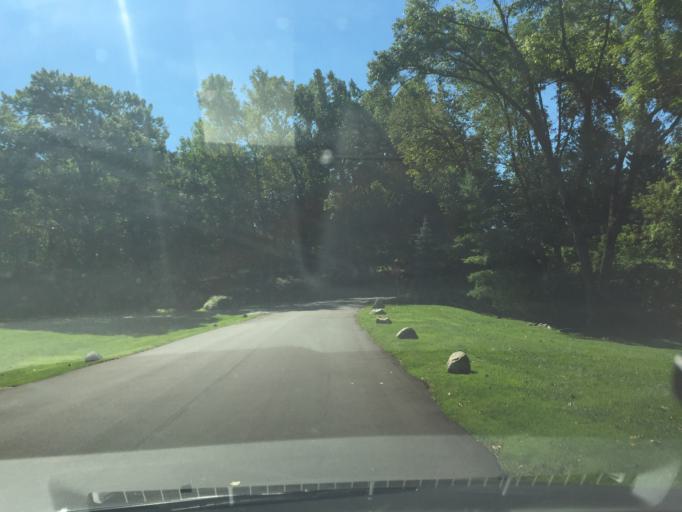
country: US
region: Michigan
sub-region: Oakland County
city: Franklin
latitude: 42.5676
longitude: -83.2955
